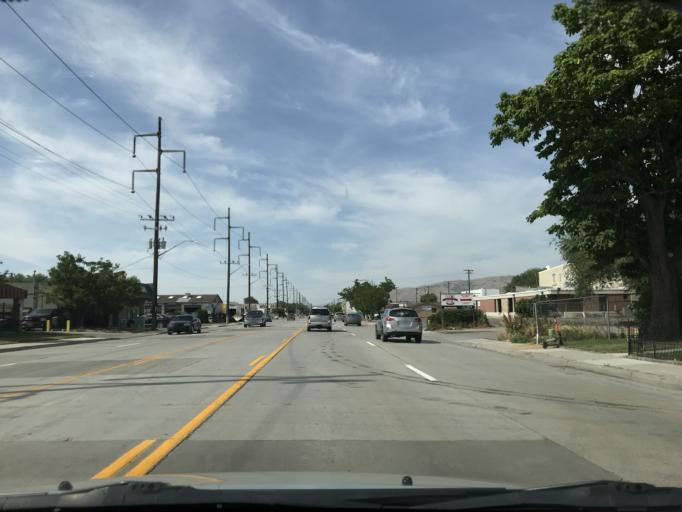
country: US
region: Utah
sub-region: Salt Lake County
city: South Salt Lake
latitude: 40.7278
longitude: -111.9168
